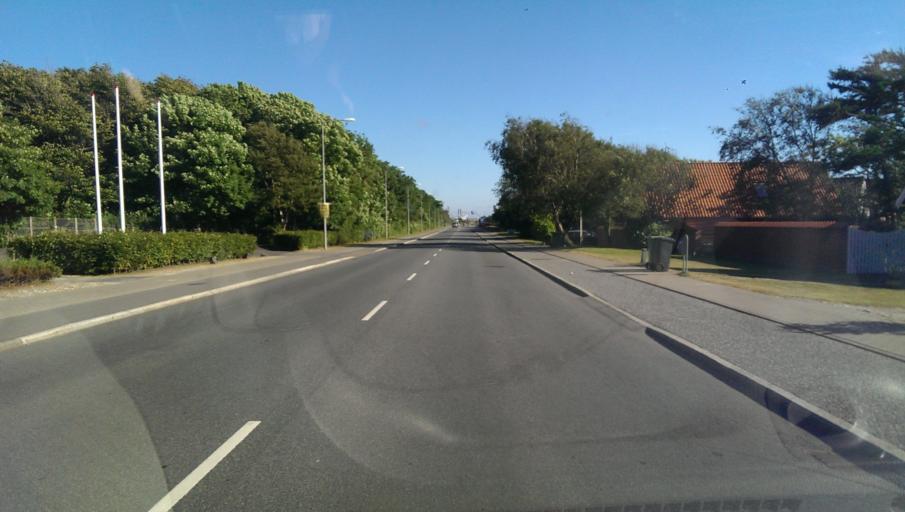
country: DK
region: South Denmark
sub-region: Esbjerg Kommune
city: Esbjerg
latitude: 55.4927
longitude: 8.4106
